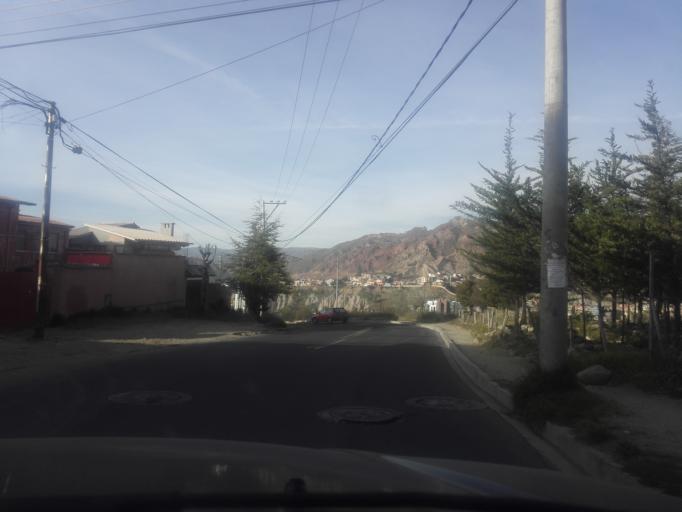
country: BO
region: La Paz
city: La Paz
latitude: -16.5241
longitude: -68.1024
